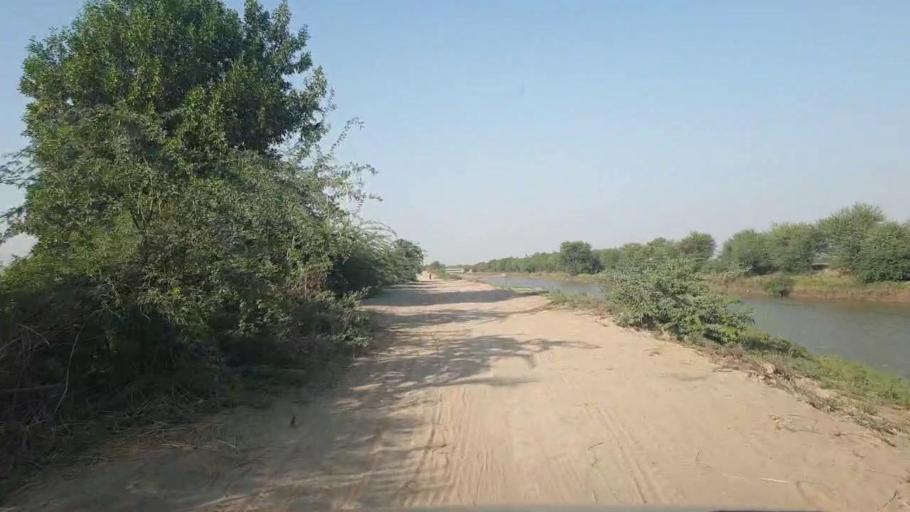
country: PK
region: Sindh
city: Badin
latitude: 24.6344
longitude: 68.8150
